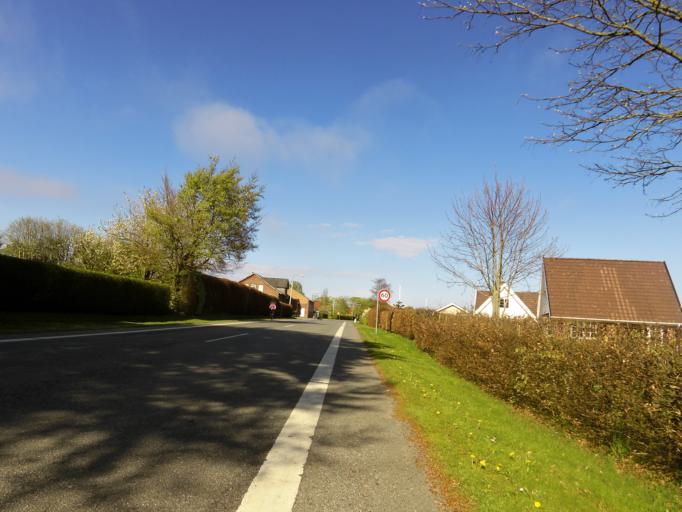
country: DK
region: South Denmark
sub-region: Tonder Kommune
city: Sherrebek
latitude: 55.1564
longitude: 8.8124
